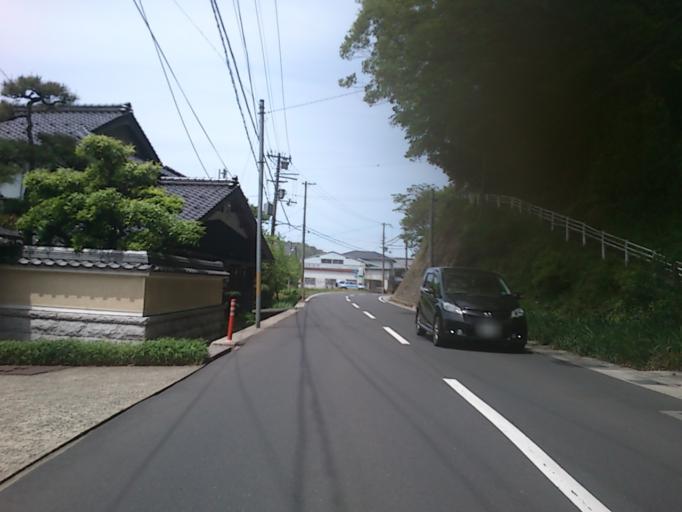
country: JP
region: Kyoto
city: Miyazu
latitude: 35.7083
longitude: 135.1055
